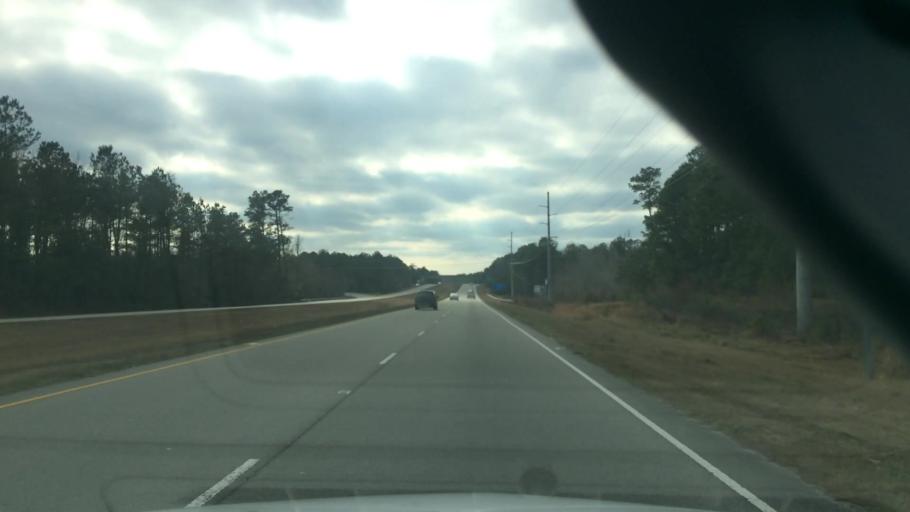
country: US
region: North Carolina
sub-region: Brunswick County
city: Shallotte
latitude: 33.9809
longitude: -78.3992
